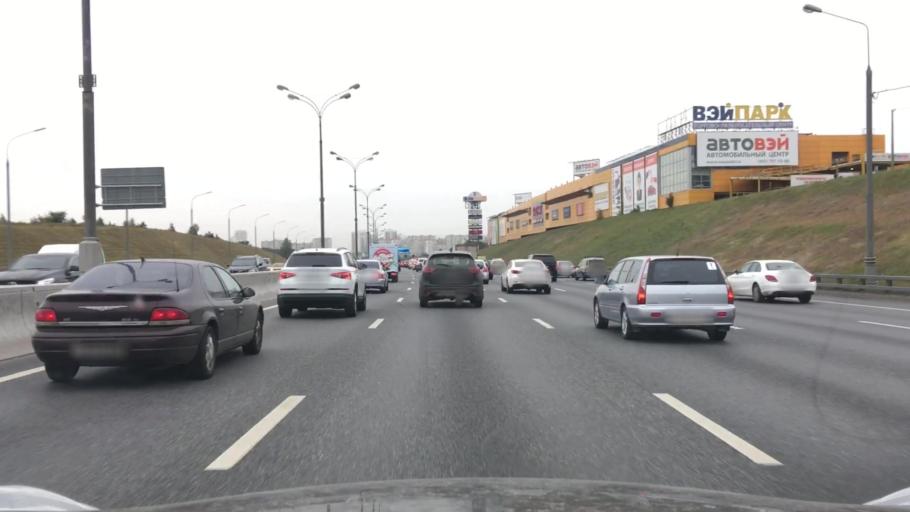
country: RU
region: Moscow
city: Strogino
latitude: 55.8603
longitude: 37.3981
